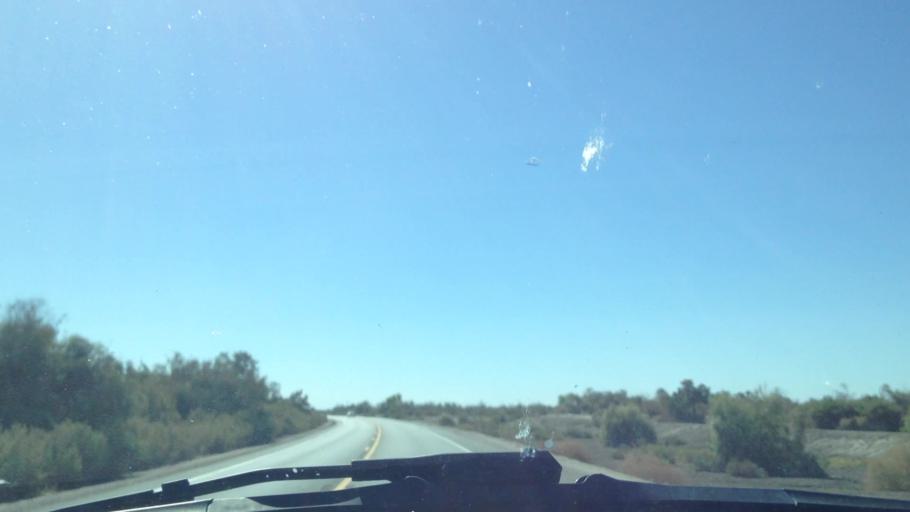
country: US
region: California
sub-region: Riverside County
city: Mecca
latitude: 33.5592
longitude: -116.0692
